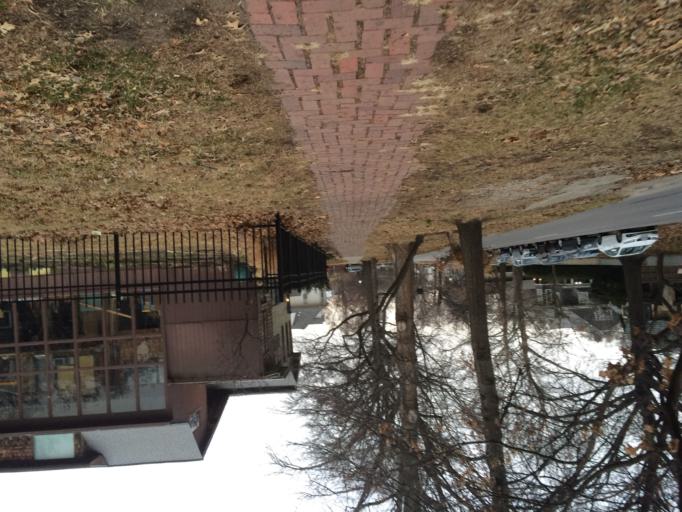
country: US
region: Kansas
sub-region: Douglas County
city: Lawrence
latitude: 38.9609
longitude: -95.2393
